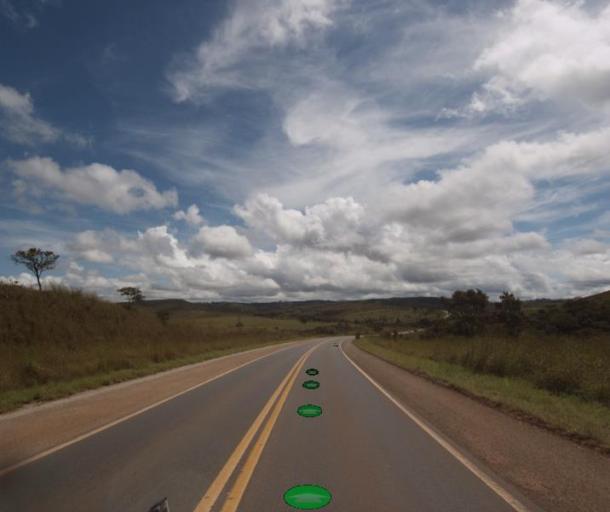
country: BR
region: Federal District
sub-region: Brasilia
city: Brasilia
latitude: -15.7539
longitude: -48.3459
